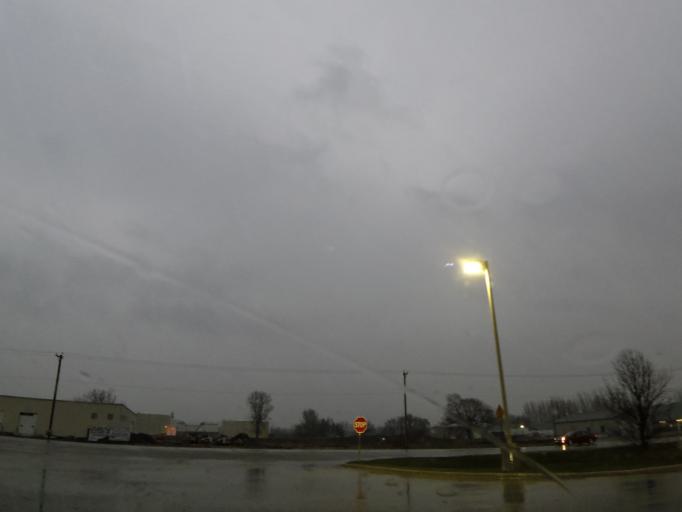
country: US
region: Iowa
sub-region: Cerro Gordo County
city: Clear Lake
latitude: 43.1333
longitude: -93.3525
